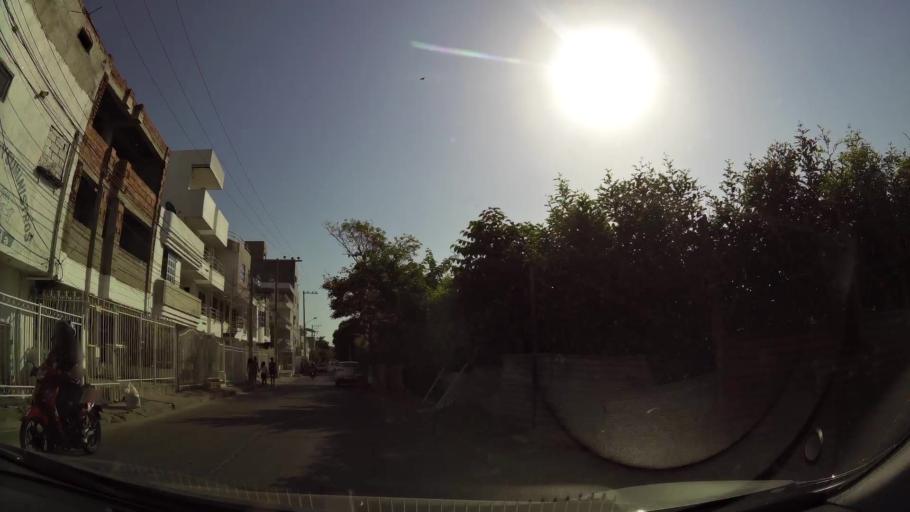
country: CO
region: Bolivar
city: Cartagena
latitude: 10.3910
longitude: -75.4976
